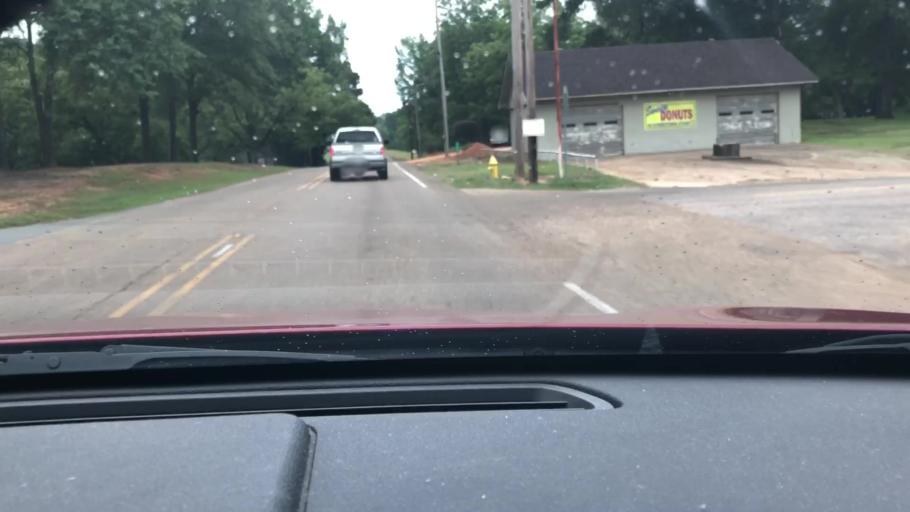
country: US
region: Arkansas
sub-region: Lafayette County
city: Stamps
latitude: 33.3658
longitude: -93.5050
